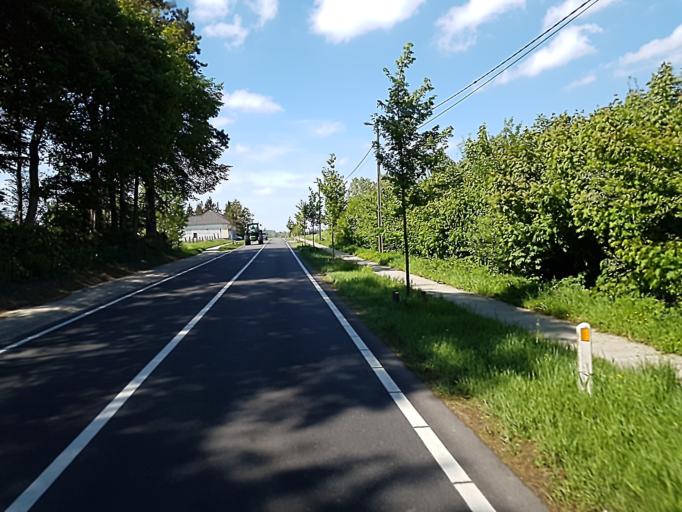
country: BE
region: Flanders
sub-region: Provincie Vlaams-Brabant
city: Glabbeek-Zuurbemde
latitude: 50.8519
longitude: 4.9036
